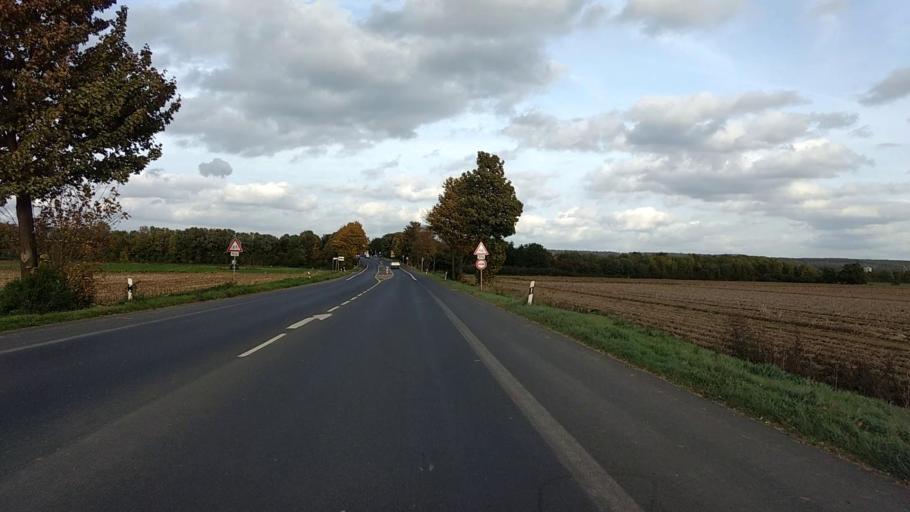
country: DE
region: North Rhine-Westphalia
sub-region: Regierungsbezirk Koln
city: Bergheim
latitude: 50.9334
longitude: 6.6438
